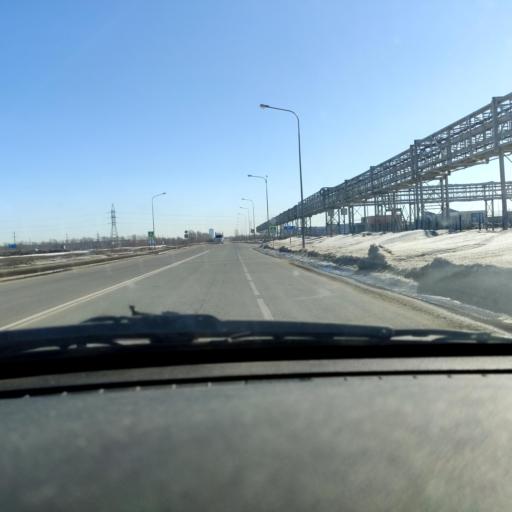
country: RU
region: Samara
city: Podstepki
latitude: 53.5594
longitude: 49.1980
